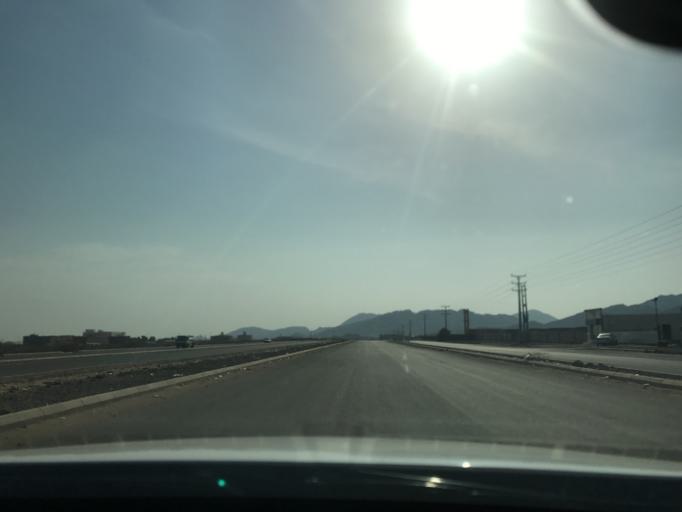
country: SA
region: Makkah
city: Al Jumum
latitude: 21.4543
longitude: 39.5460
